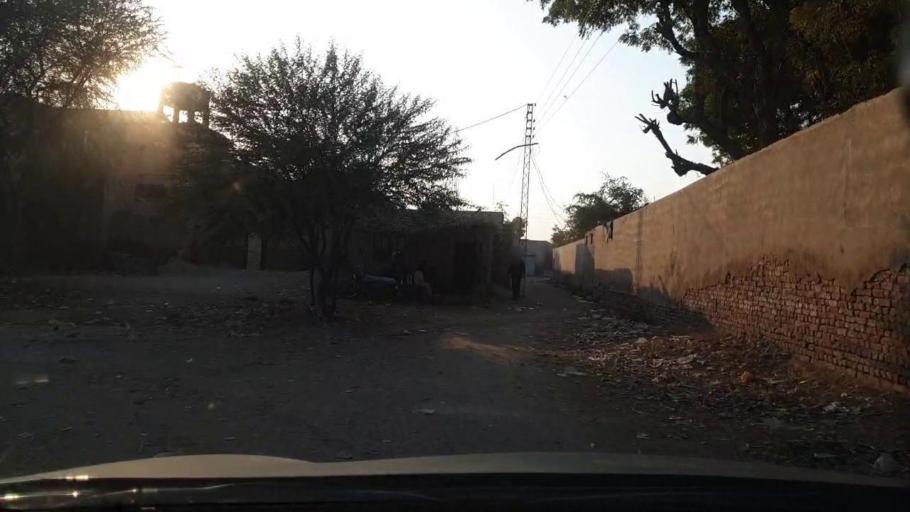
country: PK
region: Sindh
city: Tando Adam
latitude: 25.6825
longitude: 68.7448
